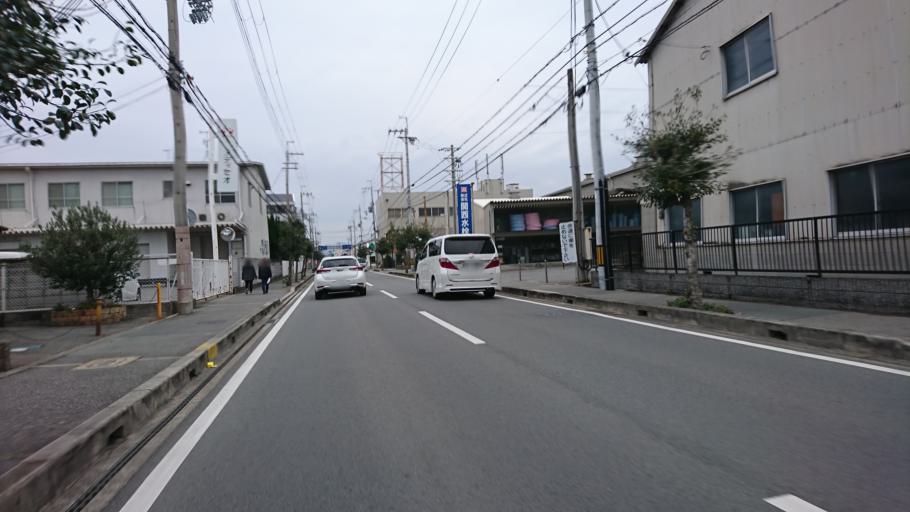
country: JP
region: Hyogo
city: Kakogawacho-honmachi
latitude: 34.7672
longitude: 134.8261
